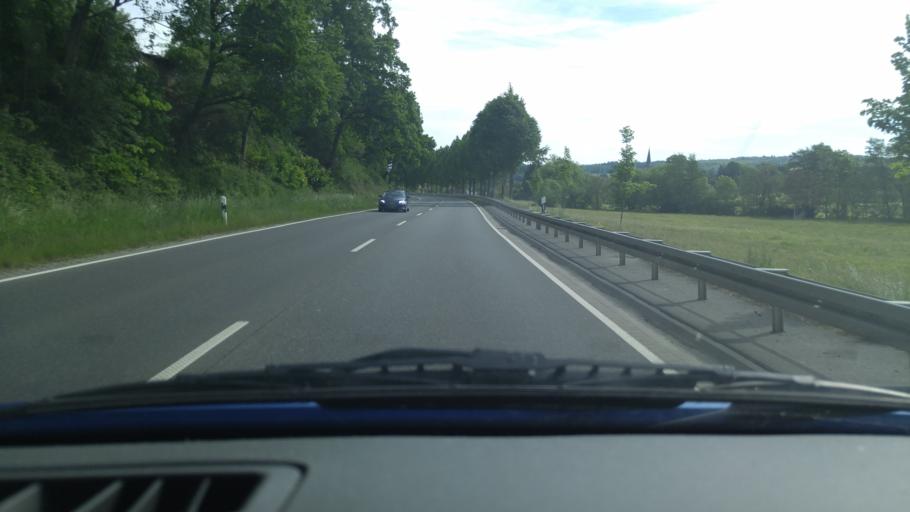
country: DE
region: Hesse
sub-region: Regierungsbezirk Giessen
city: Schotten
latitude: 50.4664
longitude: 9.0697
